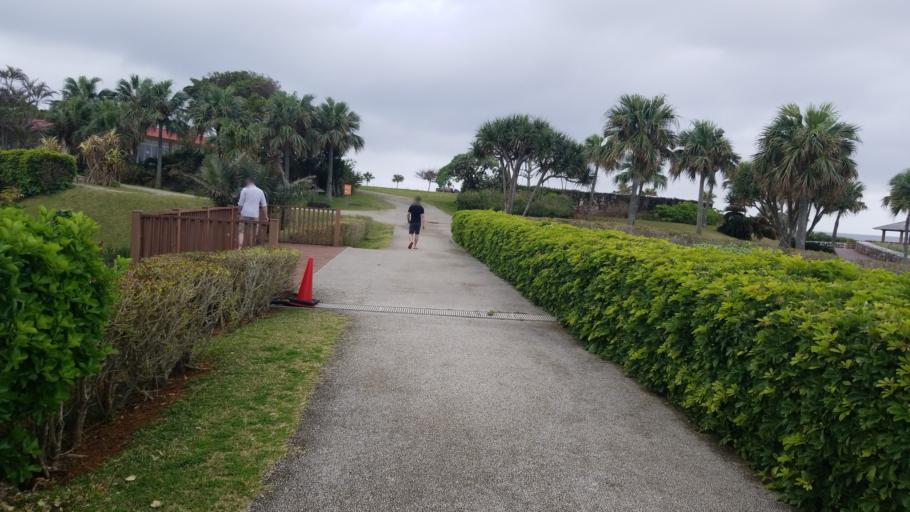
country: JP
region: Okinawa
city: Nago
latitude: 26.6924
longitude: 127.8755
